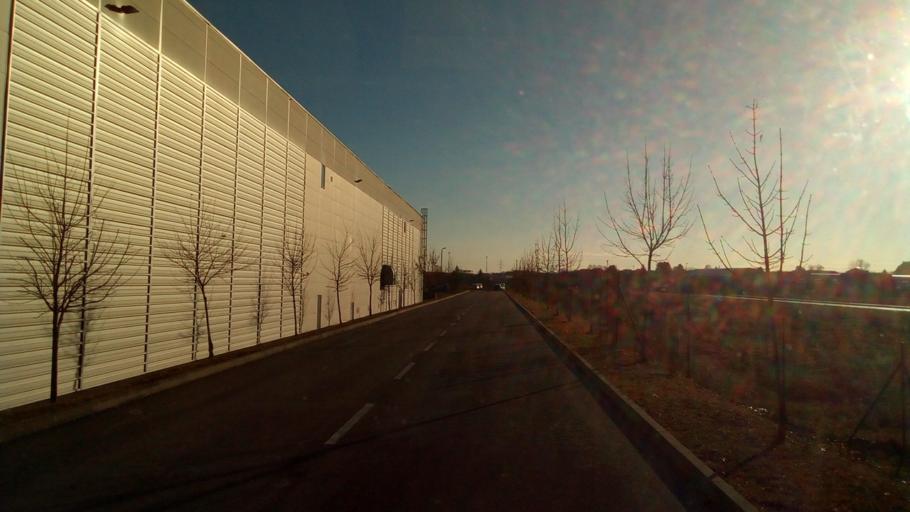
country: HR
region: Zagrebacka
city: Bestovje
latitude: 45.8022
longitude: 15.7733
